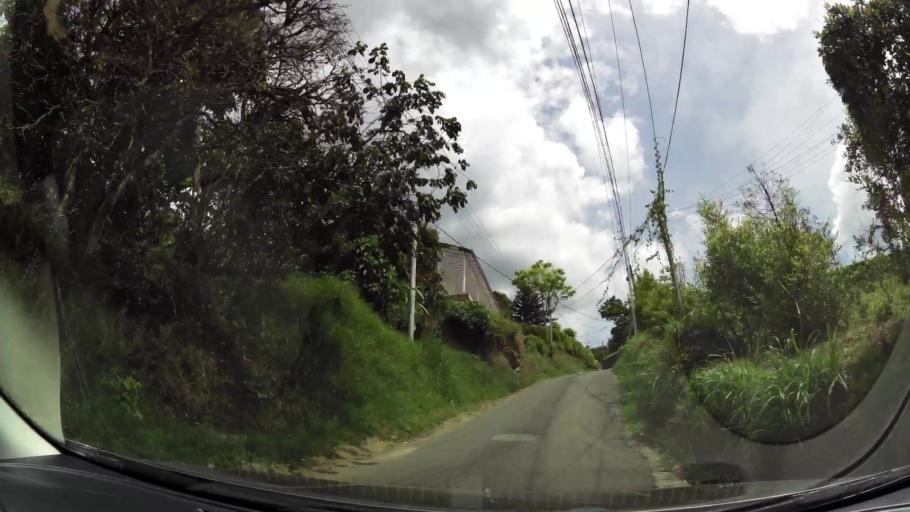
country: CO
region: Antioquia
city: Municipio de Copacabana
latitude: 6.3263
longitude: -75.4991
